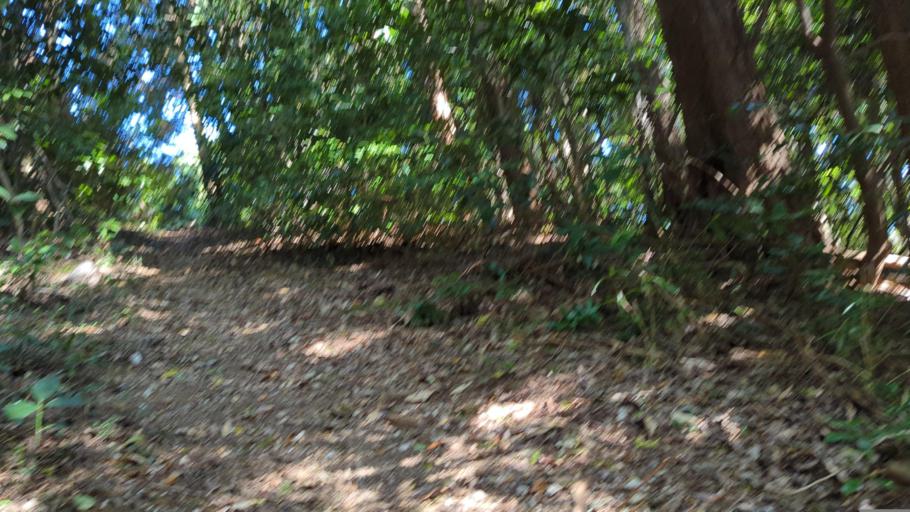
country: JP
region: Shizuoka
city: Kosai-shi
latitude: 34.7747
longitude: 137.4722
